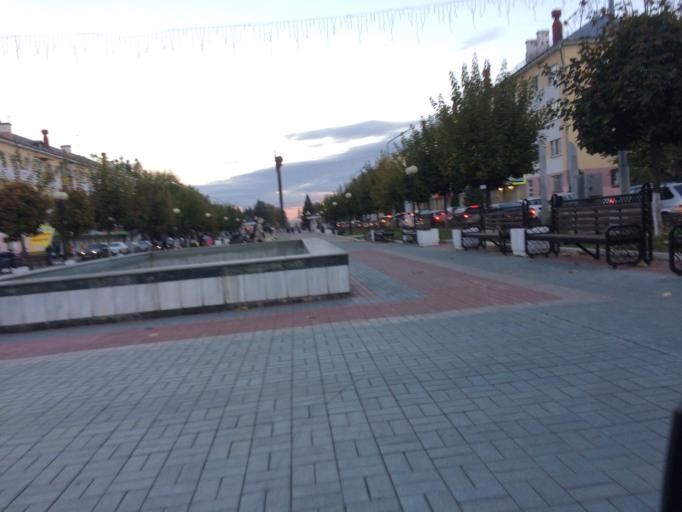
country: RU
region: Mariy-El
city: Yoshkar-Ola
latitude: 56.6377
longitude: 47.8840
